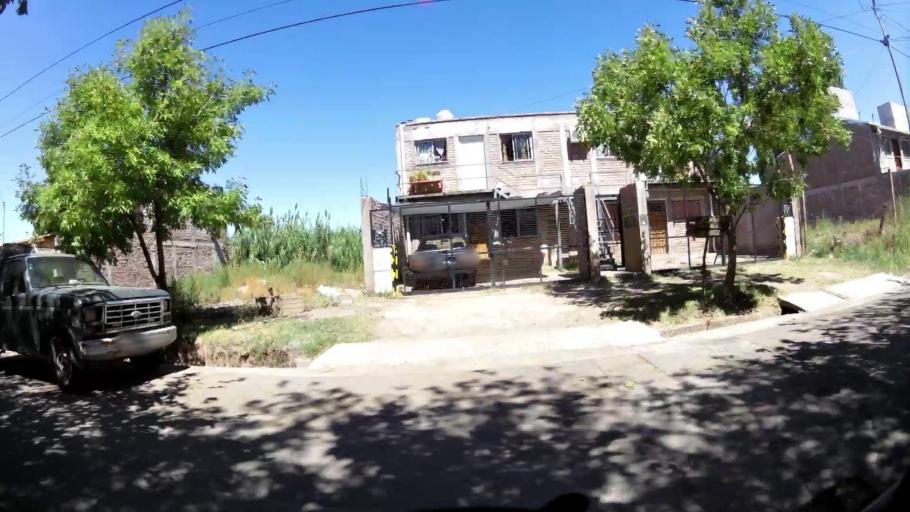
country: AR
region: Mendoza
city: Las Heras
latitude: -32.8542
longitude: -68.8488
